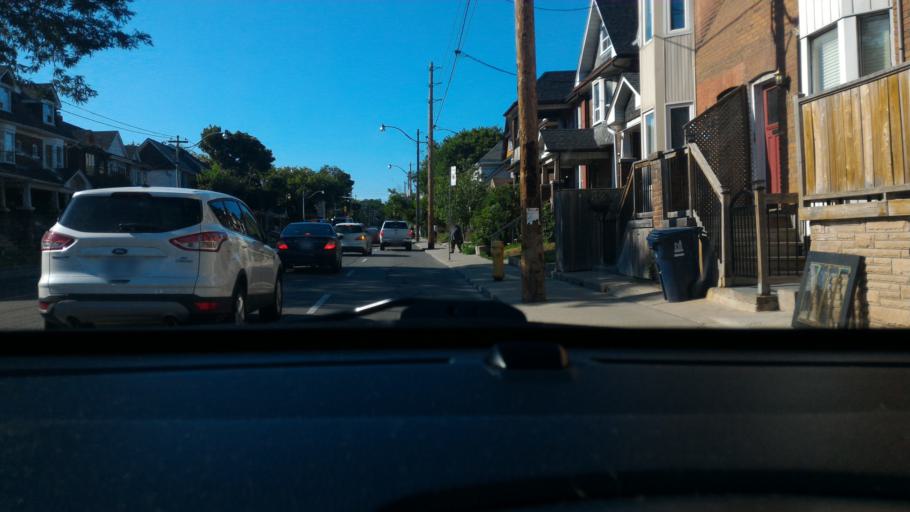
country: CA
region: Ontario
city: Scarborough
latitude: 43.6722
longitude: -79.3071
